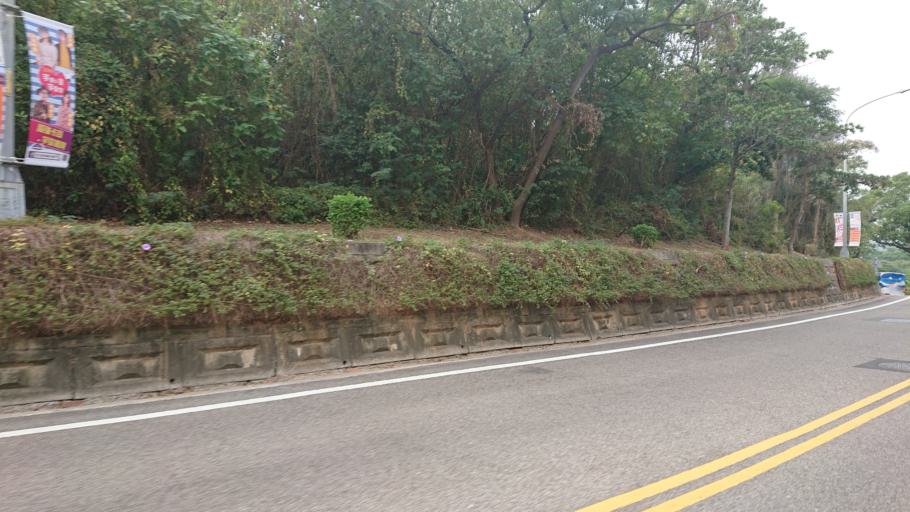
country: TW
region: Fukien
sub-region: Kinmen
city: Jincheng
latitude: 24.4270
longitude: 118.2549
